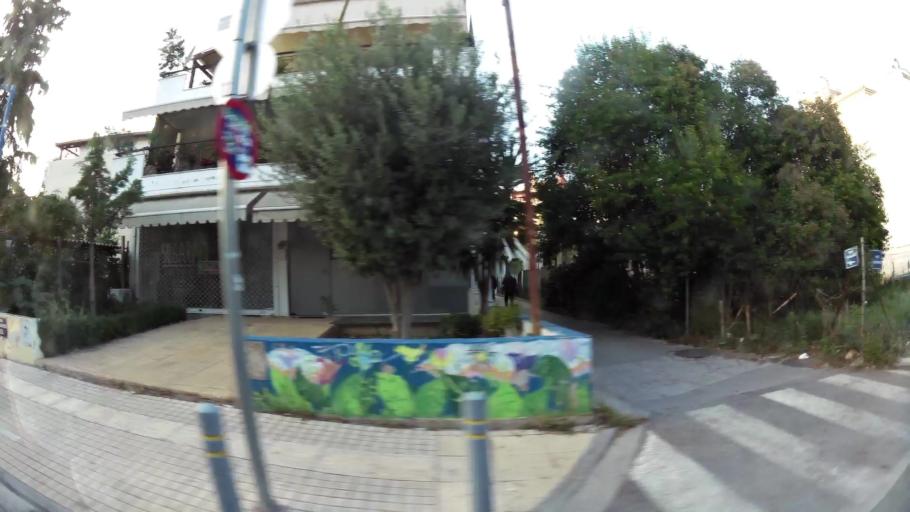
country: GR
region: Attica
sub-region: Nomarchia Athinas
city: Agia Paraskevi
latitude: 38.0183
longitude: 23.8273
